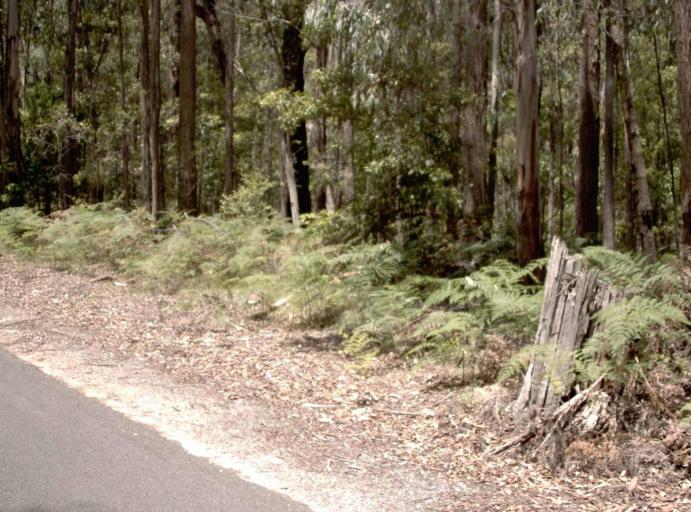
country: AU
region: New South Wales
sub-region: Bombala
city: Bombala
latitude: -37.4872
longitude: 148.9295
